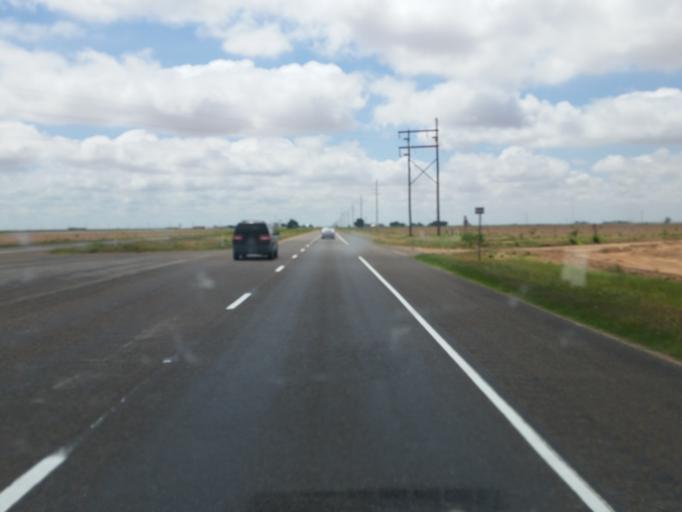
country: US
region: Texas
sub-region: Lubbock County
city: Slaton
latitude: 33.4093
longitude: -101.6258
